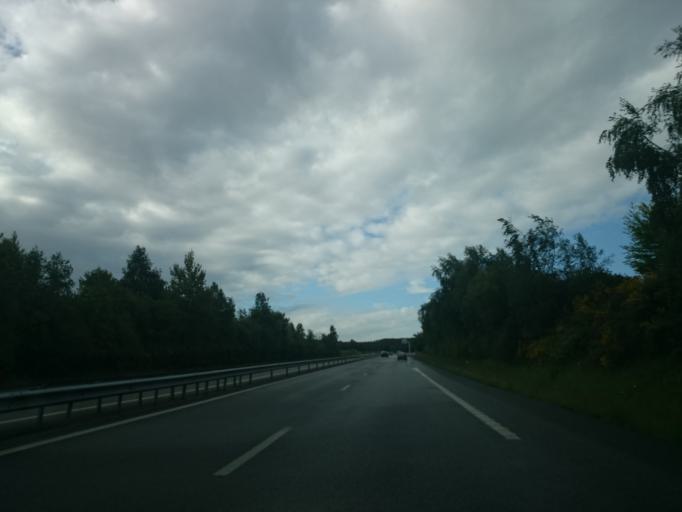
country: FR
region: Brittany
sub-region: Departement du Morbihan
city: Malestroit
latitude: 47.8253
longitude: -2.4338
